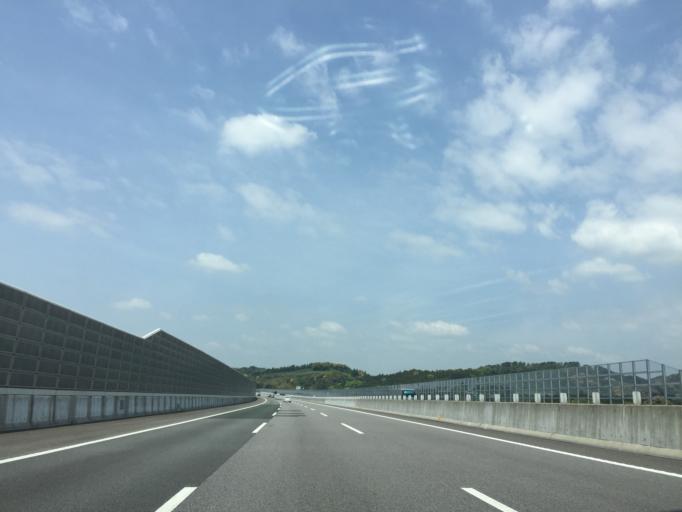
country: JP
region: Shizuoka
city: Hamakita
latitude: 34.8376
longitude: 137.8020
